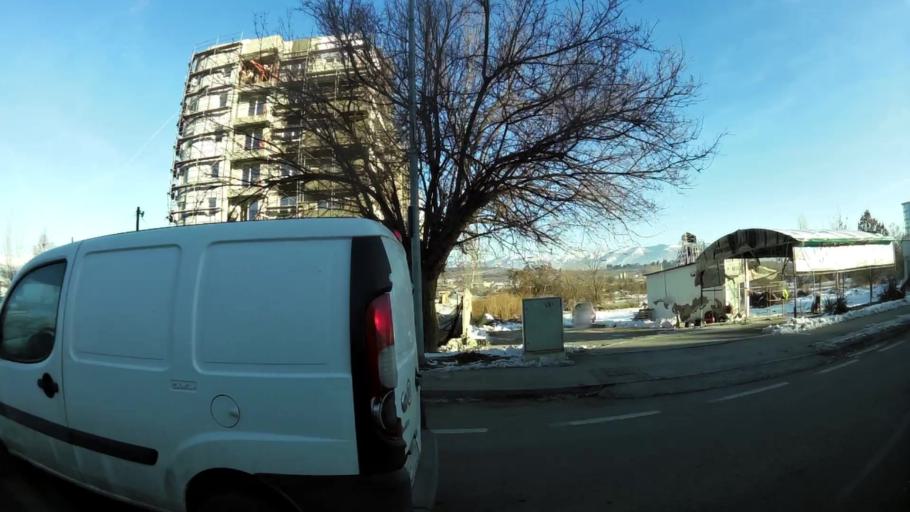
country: MK
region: Karpos
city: Skopje
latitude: 42.0079
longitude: 21.3917
